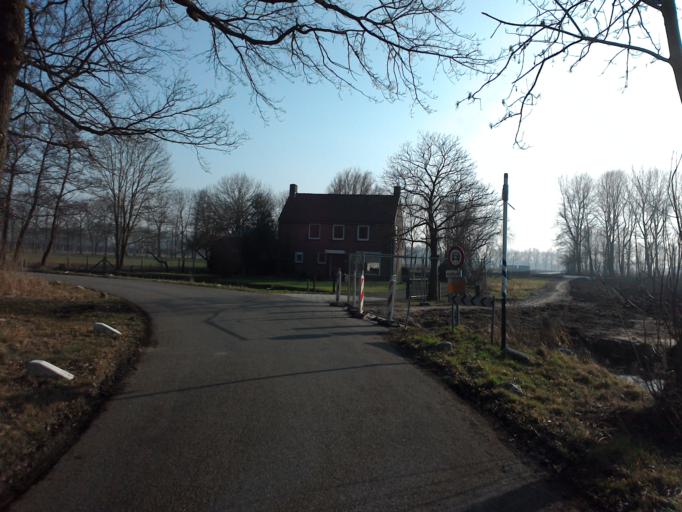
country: NL
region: Utrecht
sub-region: Gemeente Bunnik
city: Bunnik
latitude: 52.0864
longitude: 5.1898
